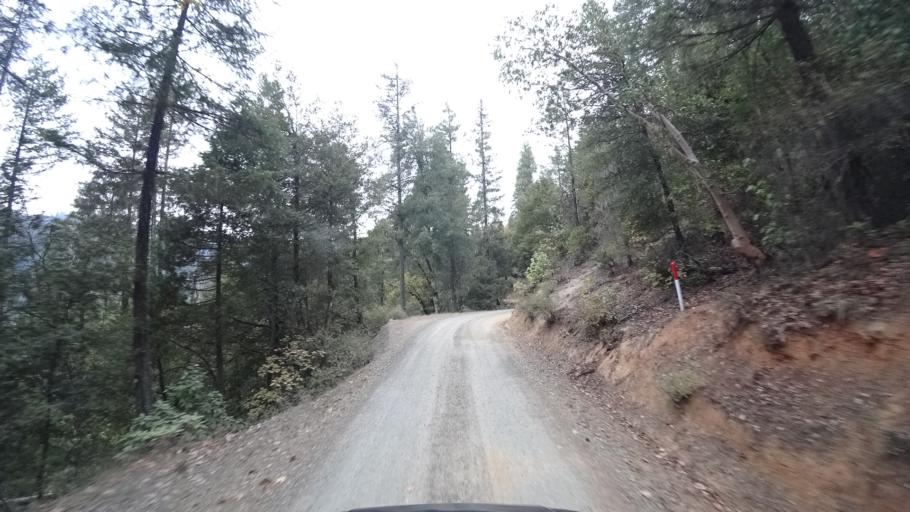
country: US
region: California
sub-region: Siskiyou County
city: Happy Camp
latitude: 41.7843
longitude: -123.3343
